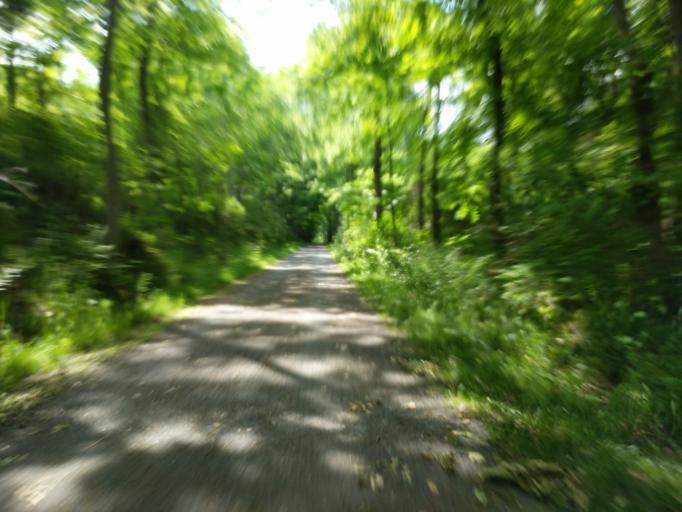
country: US
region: New York
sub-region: Tompkins County
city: Trumansburg
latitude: 42.5303
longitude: -76.6076
